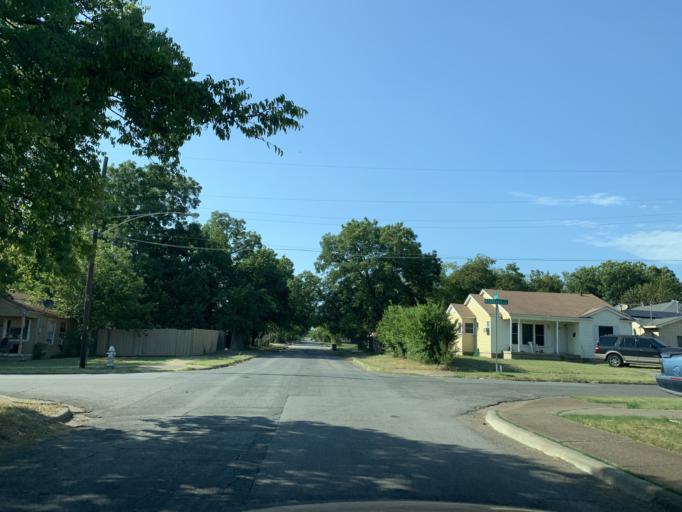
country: US
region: Texas
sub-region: Dallas County
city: Dallas
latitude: 32.7043
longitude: -96.7922
